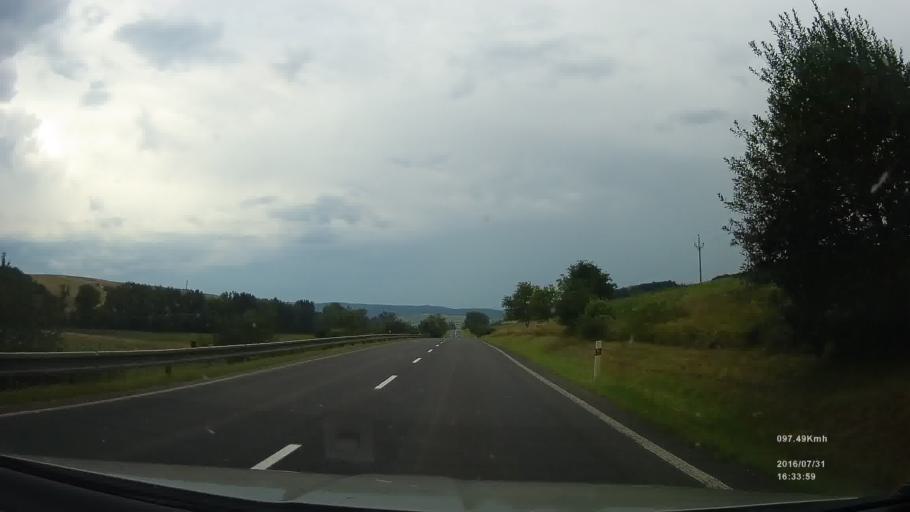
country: SK
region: Presovsky
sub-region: Okres Bardejov
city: Bardejov
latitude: 49.1751
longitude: 21.3065
